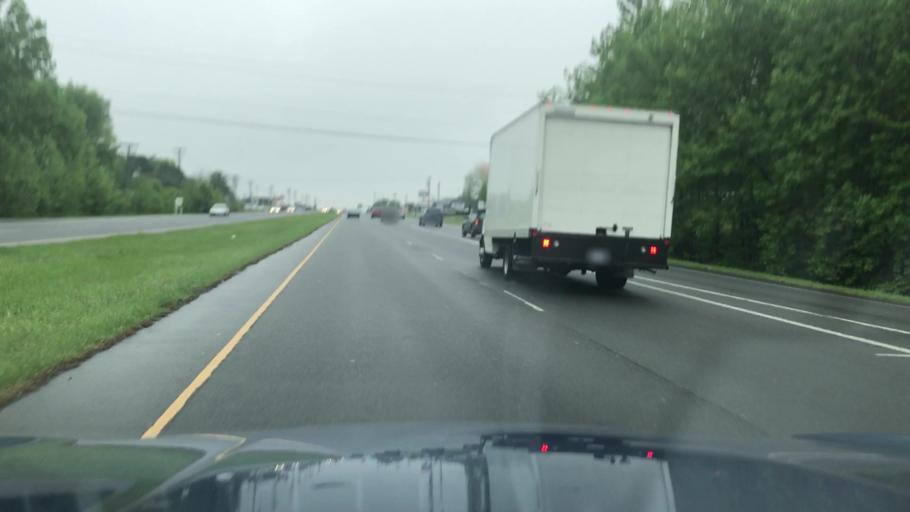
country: US
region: North Carolina
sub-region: Mecklenburg County
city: Matthews
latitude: 35.1225
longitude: -80.7019
